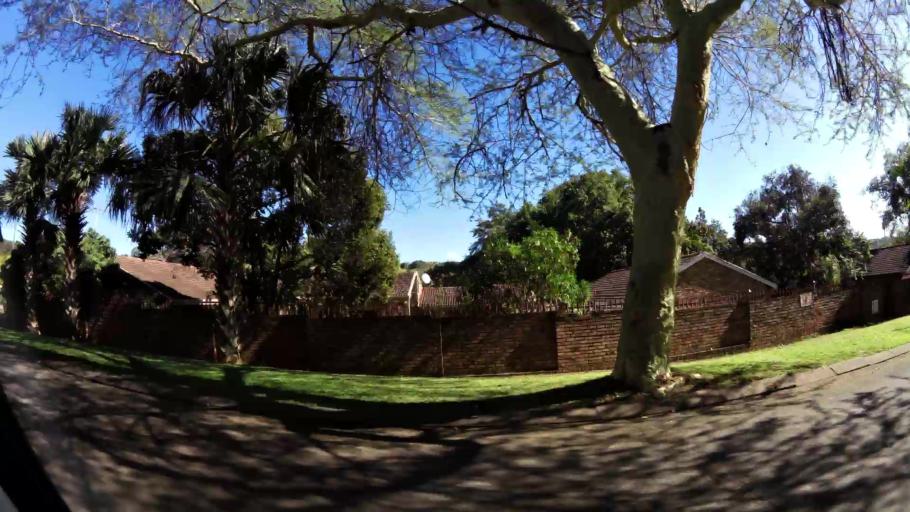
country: ZA
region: Limpopo
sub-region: Mopani District Municipality
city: Tzaneen
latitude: -23.8356
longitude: 30.1468
